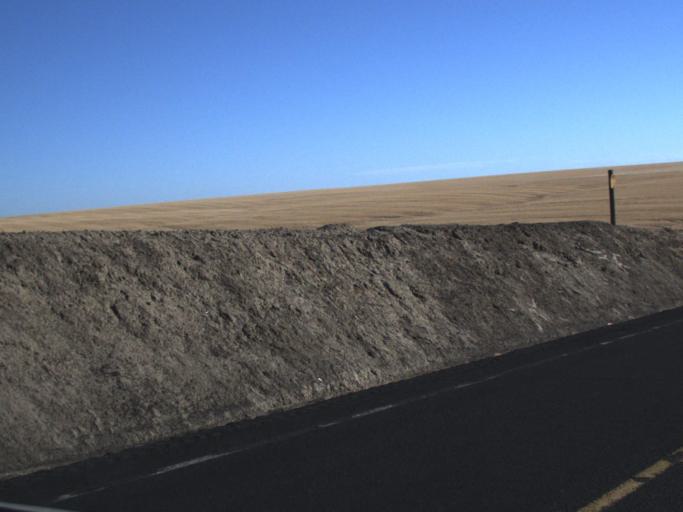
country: US
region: Washington
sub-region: Adams County
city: Ritzville
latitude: 47.0888
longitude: -118.3654
